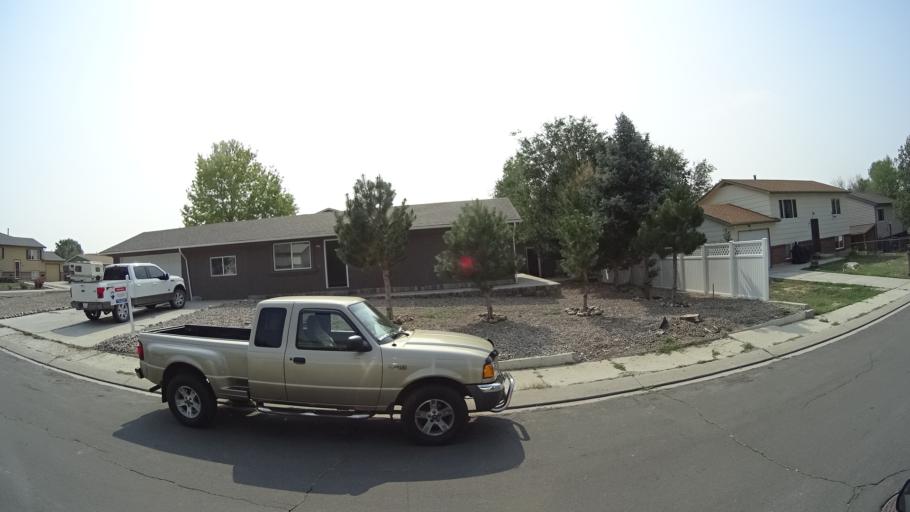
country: US
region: Colorado
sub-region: El Paso County
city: Stratmoor
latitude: 38.8072
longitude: -104.7612
